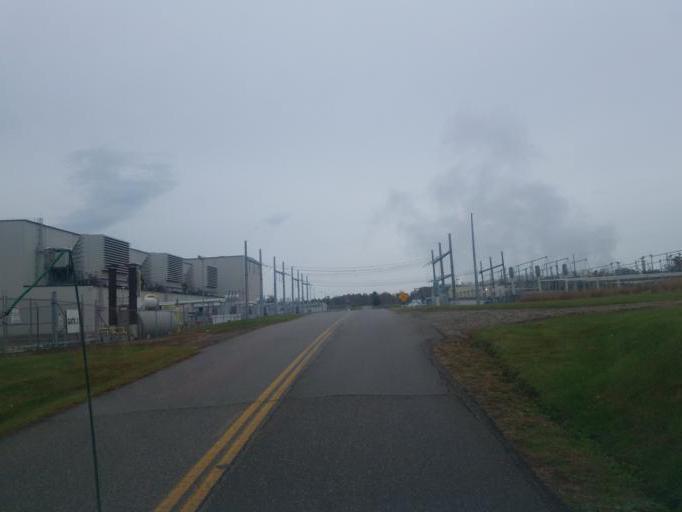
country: US
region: Ohio
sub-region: Washington County
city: Beverly
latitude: 39.5316
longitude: -81.7162
